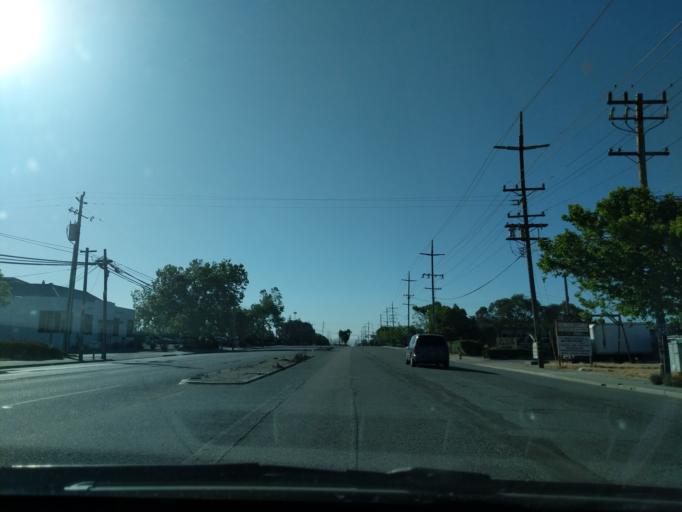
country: US
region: California
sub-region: Monterey County
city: Salinas
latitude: 36.6559
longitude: -121.6328
